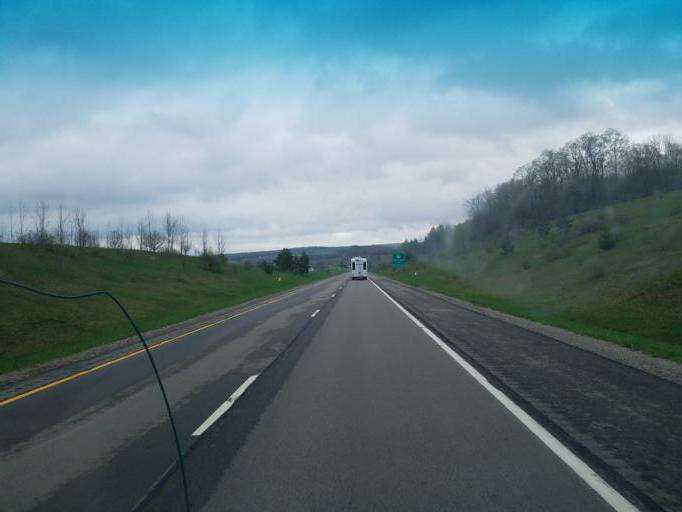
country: US
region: New York
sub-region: Chautauqua County
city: Clymer
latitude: 42.1463
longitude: -79.6230
